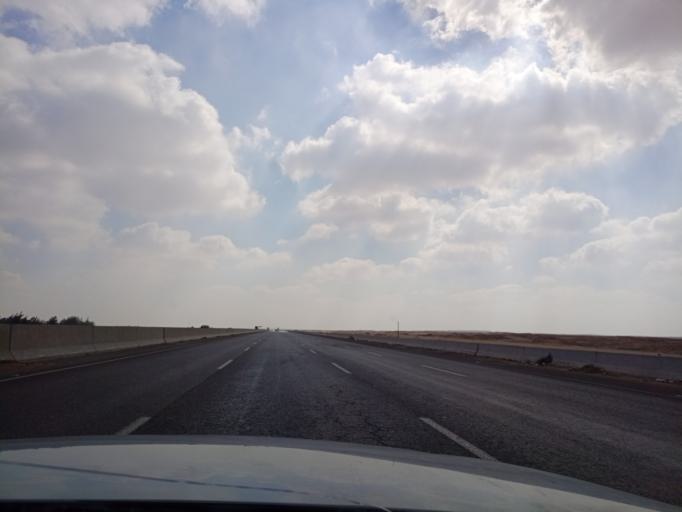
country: EG
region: Eastern Province
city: Bilbays
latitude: 30.3256
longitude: 31.5585
